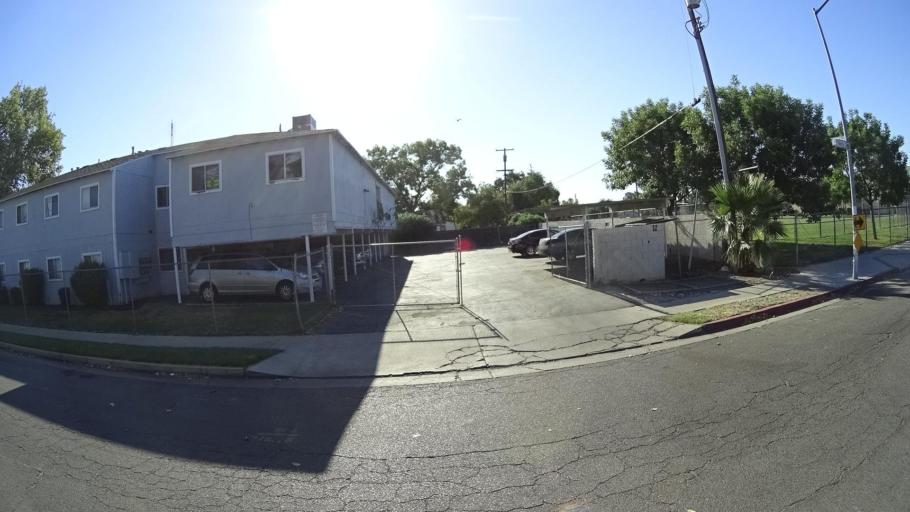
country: US
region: California
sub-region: Fresno County
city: Fresno
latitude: 36.7488
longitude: -119.7839
